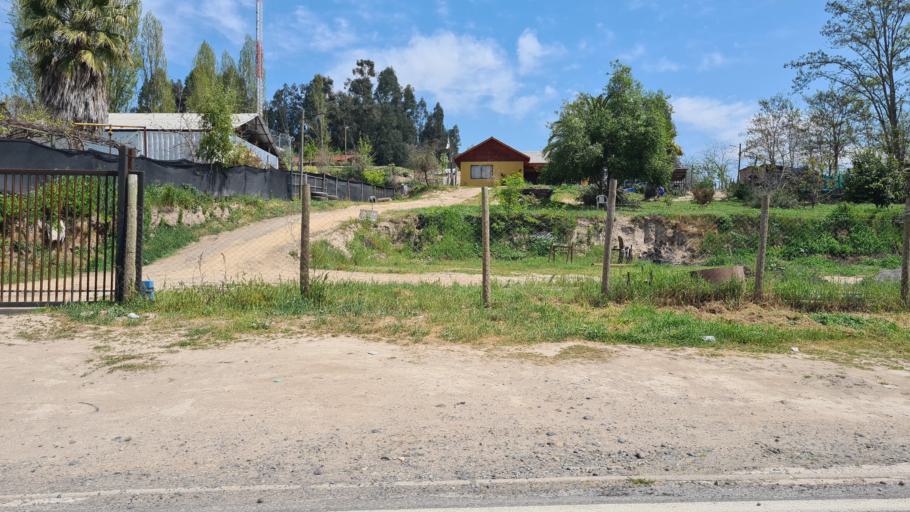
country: CL
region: O'Higgins
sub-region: Provincia de Cachapoal
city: San Vicente
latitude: -34.1715
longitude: -71.4069
